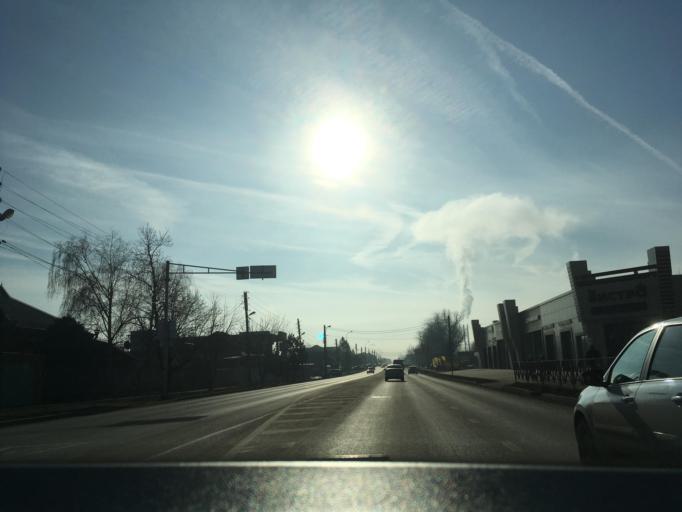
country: RU
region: Krasnodarskiy
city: Krasnodar
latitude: 45.0993
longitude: 39.0133
